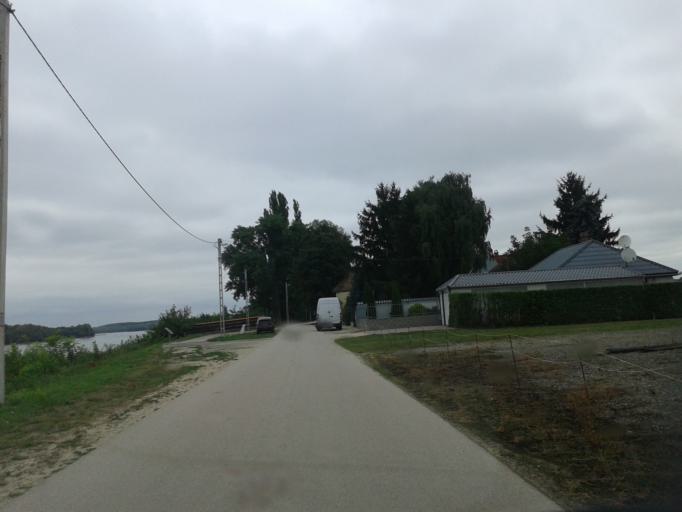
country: HU
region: Bacs-Kiskun
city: Harta
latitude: 46.6979
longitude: 19.0116
